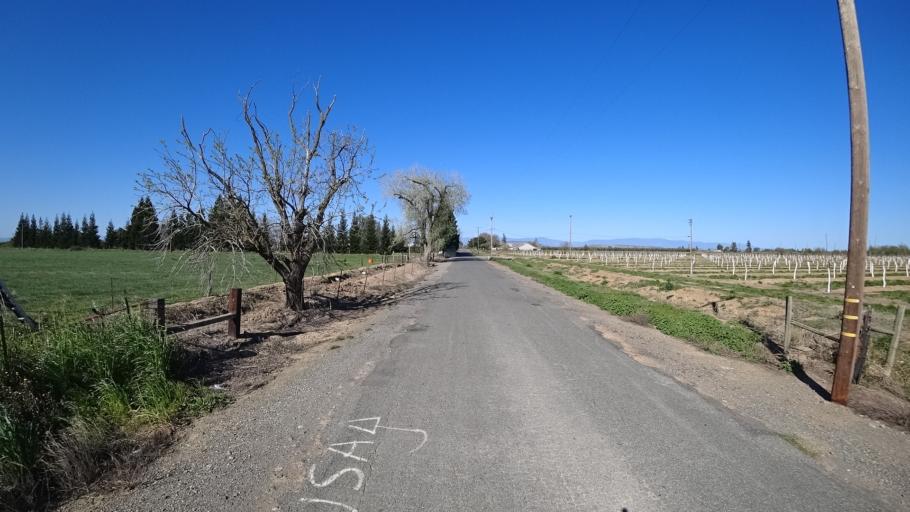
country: US
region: California
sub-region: Glenn County
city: Orland
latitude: 39.7369
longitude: -122.2251
